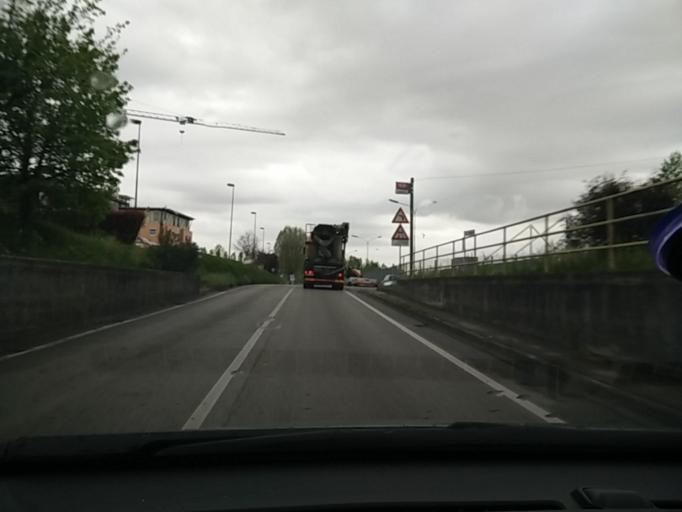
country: IT
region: Veneto
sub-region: Provincia di Treviso
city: Silea
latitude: 45.6505
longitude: 12.3032
